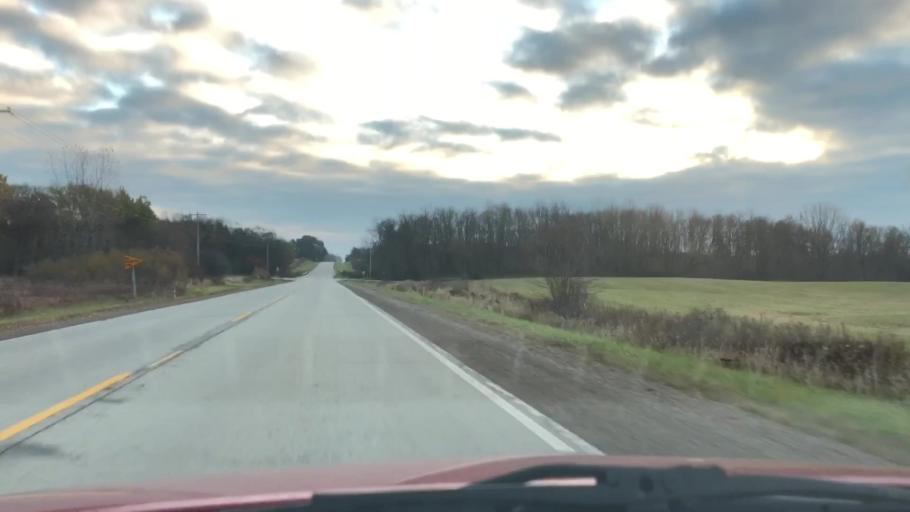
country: US
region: Wisconsin
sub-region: Brown County
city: Oneida
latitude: 44.4443
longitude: -88.2537
